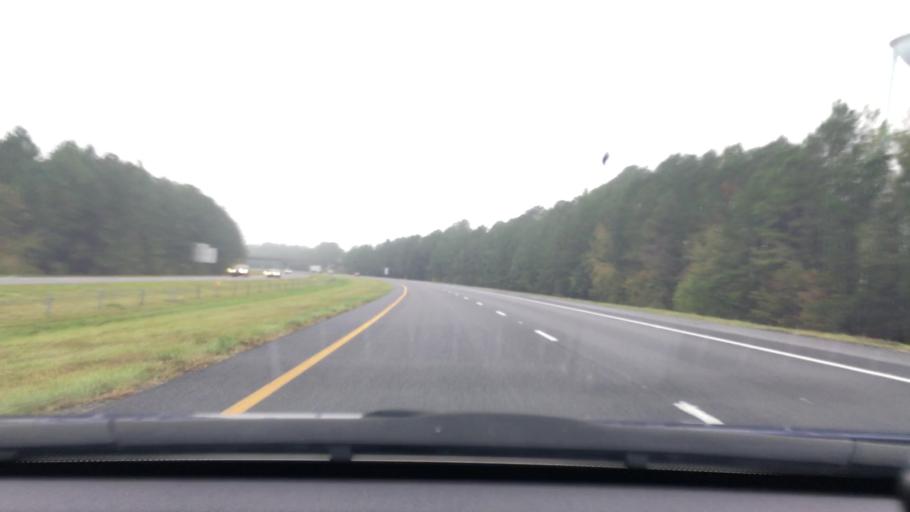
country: US
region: South Carolina
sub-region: Florence County
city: Timmonsville
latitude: 34.2082
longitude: -80.0357
